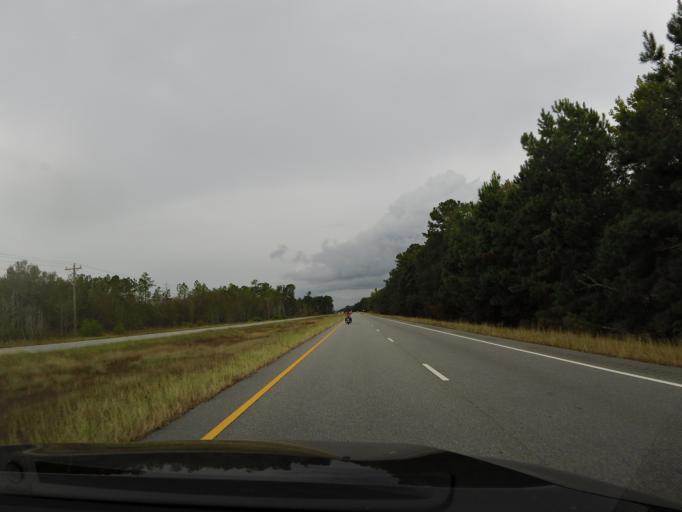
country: US
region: Georgia
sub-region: McIntosh County
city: Darien
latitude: 31.3665
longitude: -81.6220
